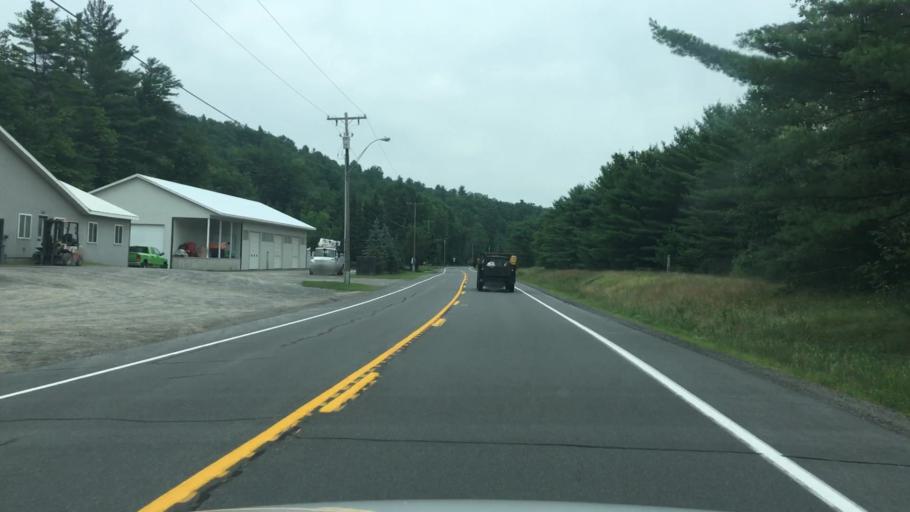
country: US
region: New York
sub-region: Clinton County
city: Peru
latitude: 44.4450
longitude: -73.6596
